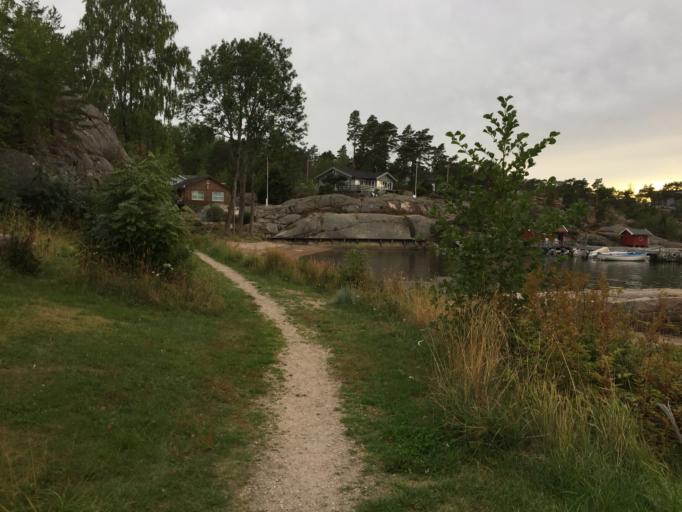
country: NO
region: Ostfold
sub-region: Hvaler
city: Skjaerhalden
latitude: 59.0838
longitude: 10.9972
